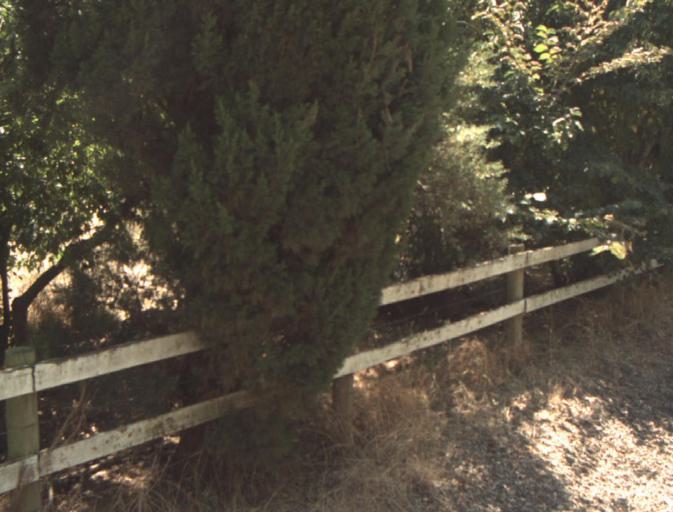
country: AU
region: Tasmania
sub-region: Launceston
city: Newstead
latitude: -41.4906
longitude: 147.2117
